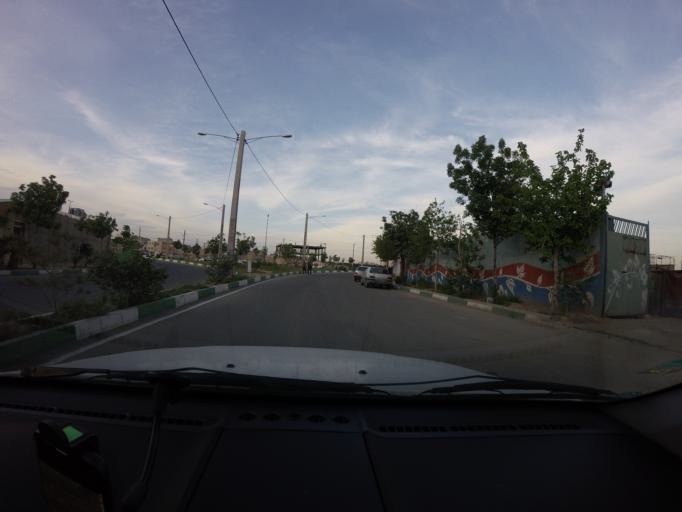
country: IR
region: Tehran
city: Eslamshahr
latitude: 35.5339
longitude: 51.2311
